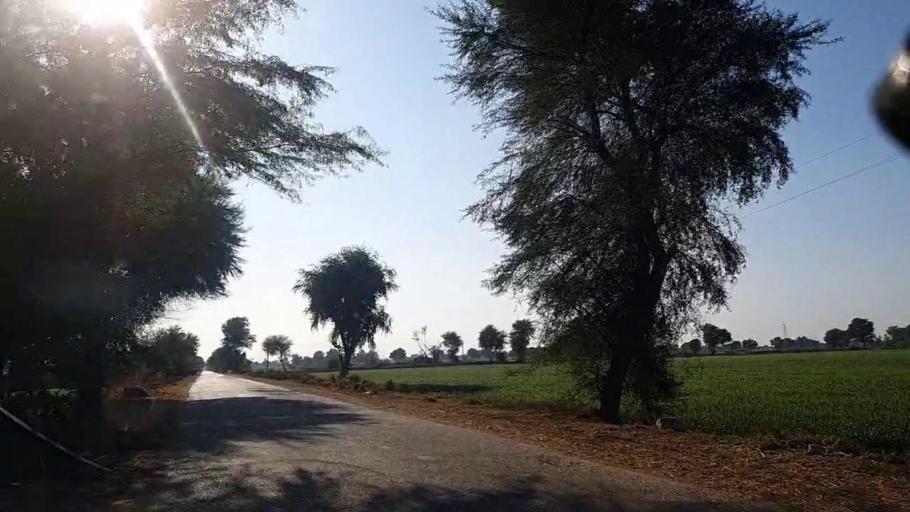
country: PK
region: Sindh
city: Khanpur
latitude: 27.7905
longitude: 69.3503
